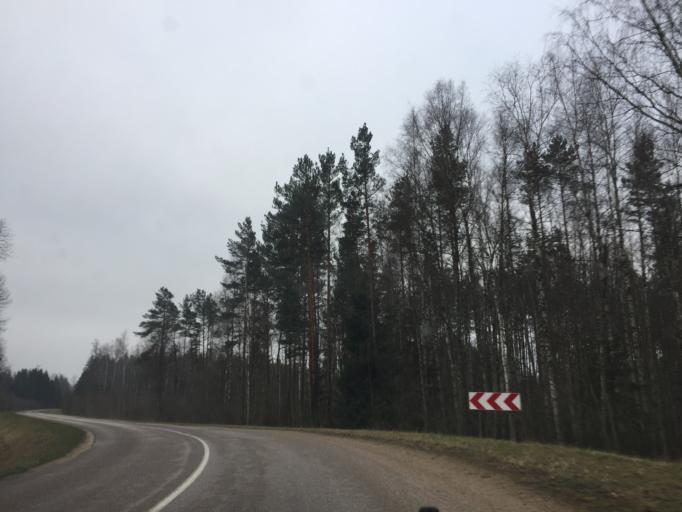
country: LV
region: Limbazu Rajons
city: Limbazi
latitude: 57.5831
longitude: 24.6591
